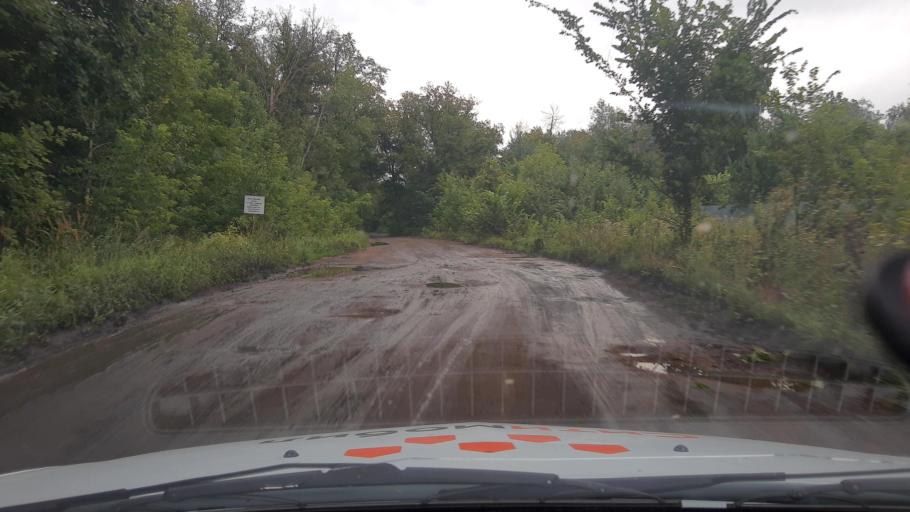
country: RU
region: Bashkortostan
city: Ufa
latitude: 54.5683
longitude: 55.9506
